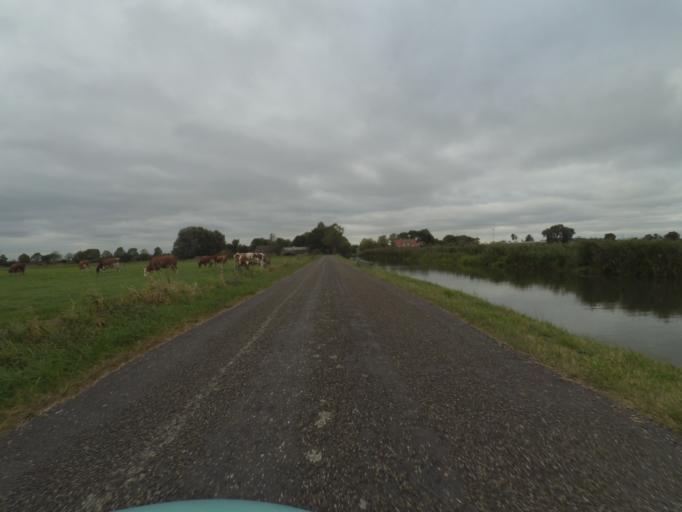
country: NL
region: Utrecht
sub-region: Gemeente Veenendaal
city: Veenendaal
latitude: 52.0099
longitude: 5.5887
